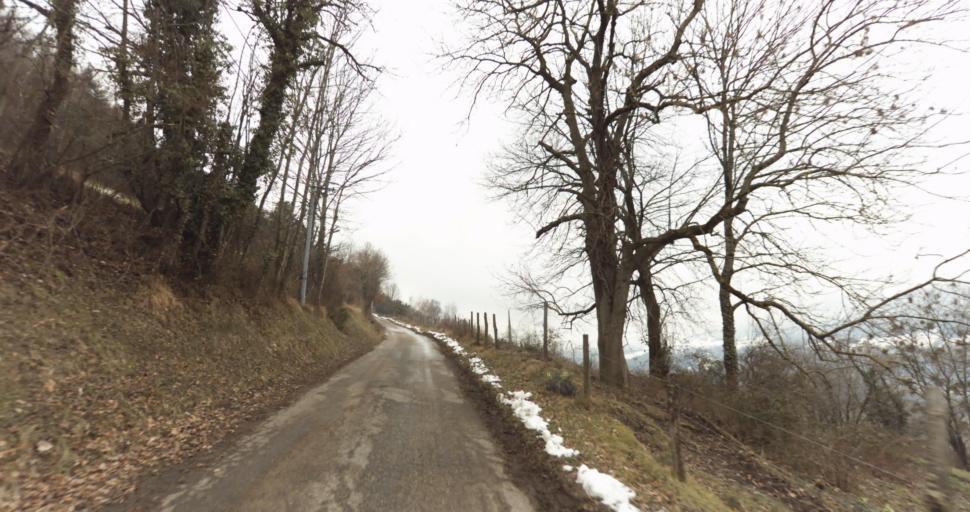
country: FR
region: Rhone-Alpes
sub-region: Departement de l'Isere
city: Vif
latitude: 45.0234
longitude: 5.6640
